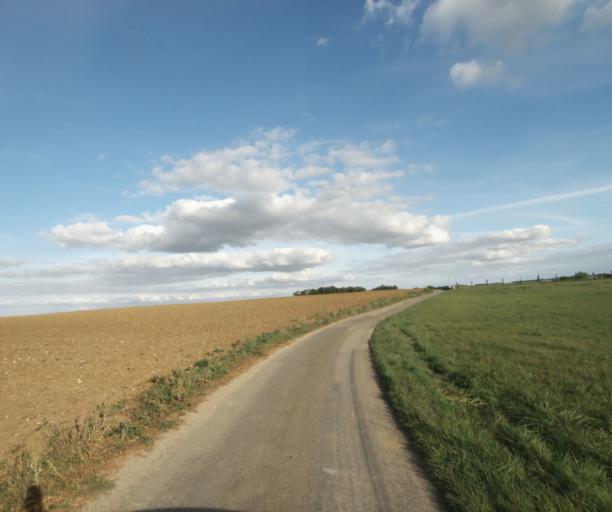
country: FR
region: Midi-Pyrenees
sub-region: Departement du Gers
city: Gondrin
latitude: 43.8960
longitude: 0.2651
